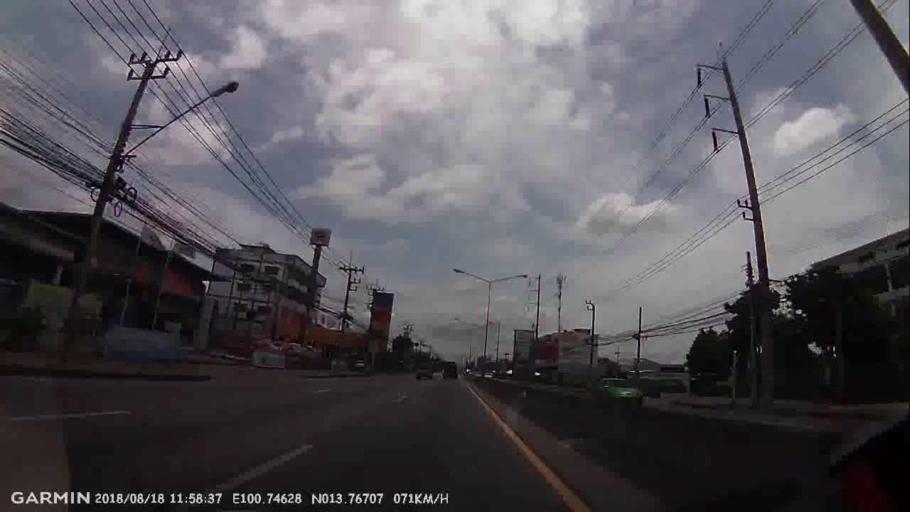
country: TH
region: Bangkok
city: Min Buri
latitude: 13.7672
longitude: 100.7462
